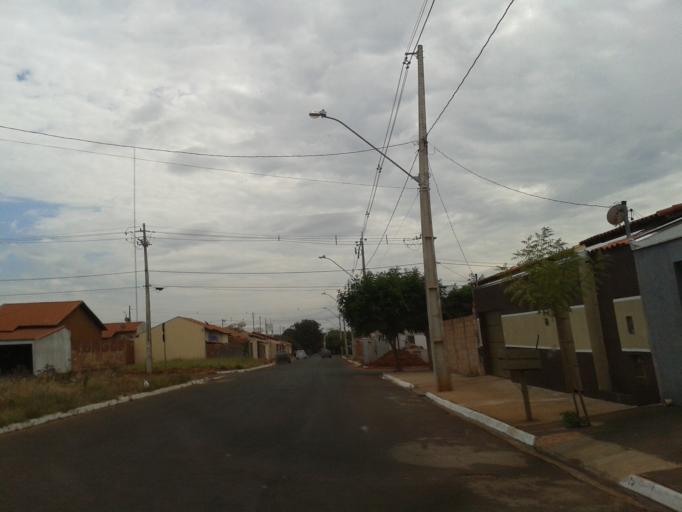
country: BR
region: Minas Gerais
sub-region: Santa Vitoria
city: Santa Vitoria
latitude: -18.8557
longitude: -50.1267
